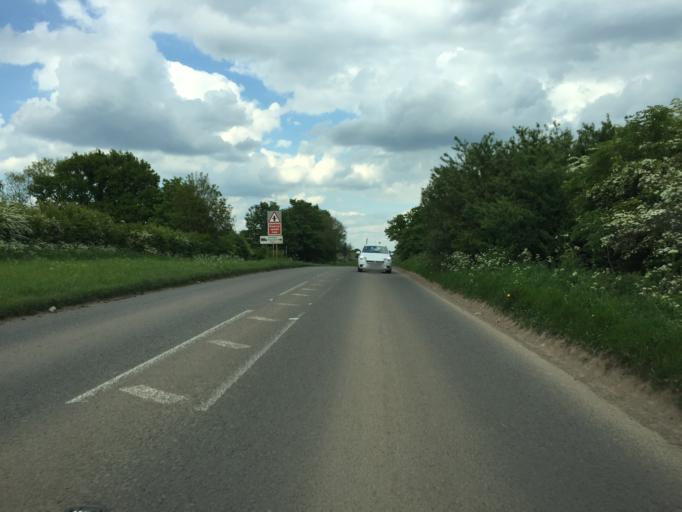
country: GB
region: England
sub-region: South Gloucestershire
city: Siston
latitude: 51.5079
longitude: -2.4649
